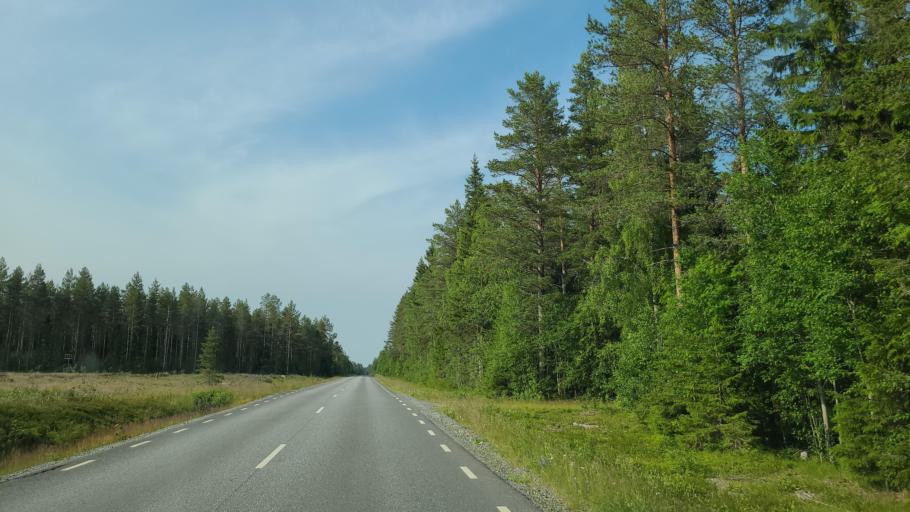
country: SE
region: Vaesterbotten
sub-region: Skelleftea Kommun
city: Burea
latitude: 64.4311
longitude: 21.3537
